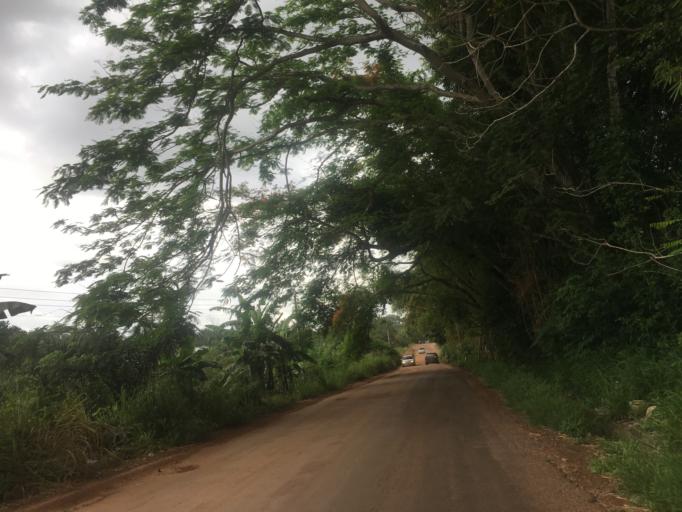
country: GH
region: Ashanti
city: Mamponteng
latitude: 6.6855
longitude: -1.5620
